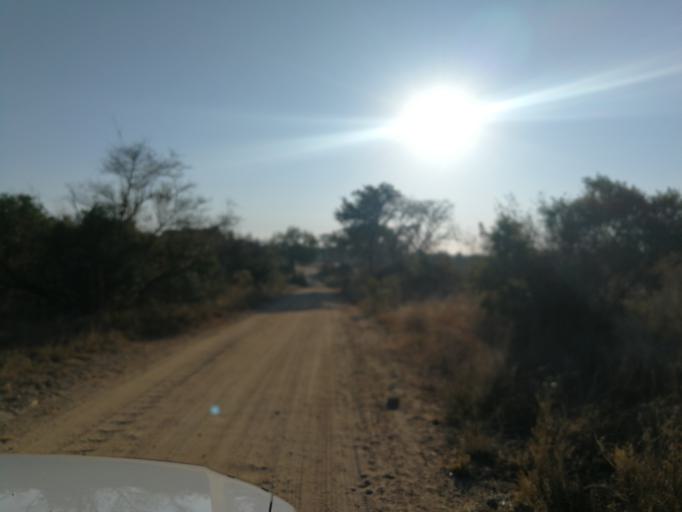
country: ZA
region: Limpopo
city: Thulamahashi
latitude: -25.0118
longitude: 31.4300
